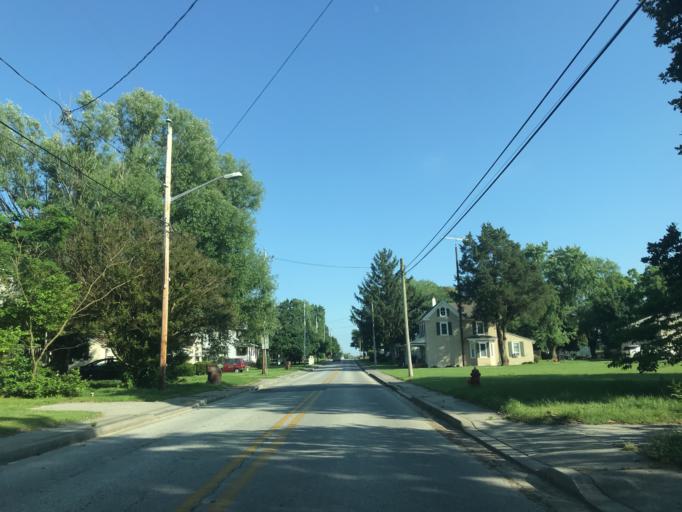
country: US
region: Maryland
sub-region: Wicomico County
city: Hebron
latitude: 38.5375
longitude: -75.7178
